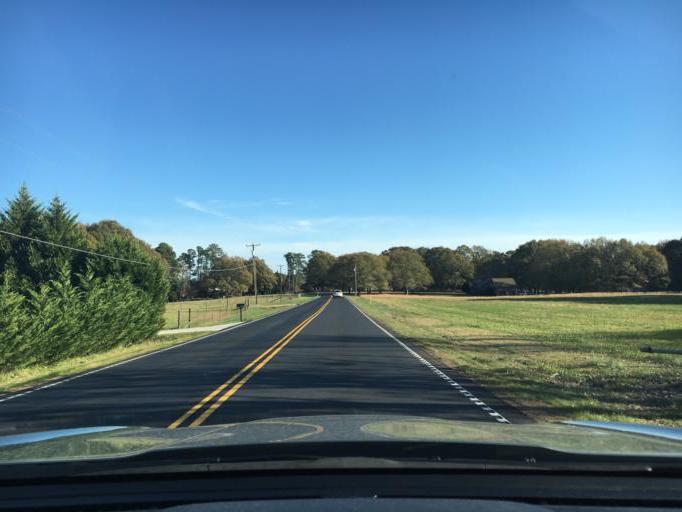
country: US
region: South Carolina
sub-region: Spartanburg County
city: Inman Mills
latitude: 35.0266
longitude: -82.0947
